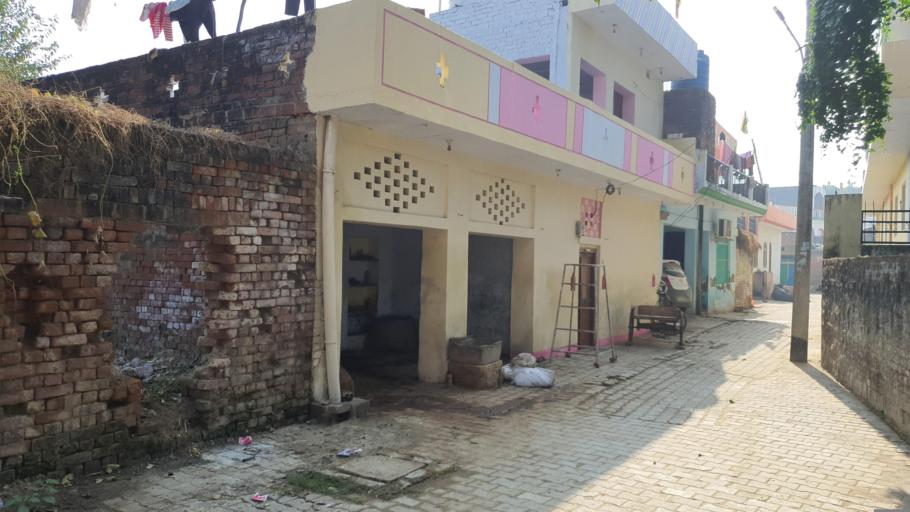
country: IN
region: Uttar Pradesh
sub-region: Lucknow District
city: Goshainganj
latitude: 26.7734
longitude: 81.0113
